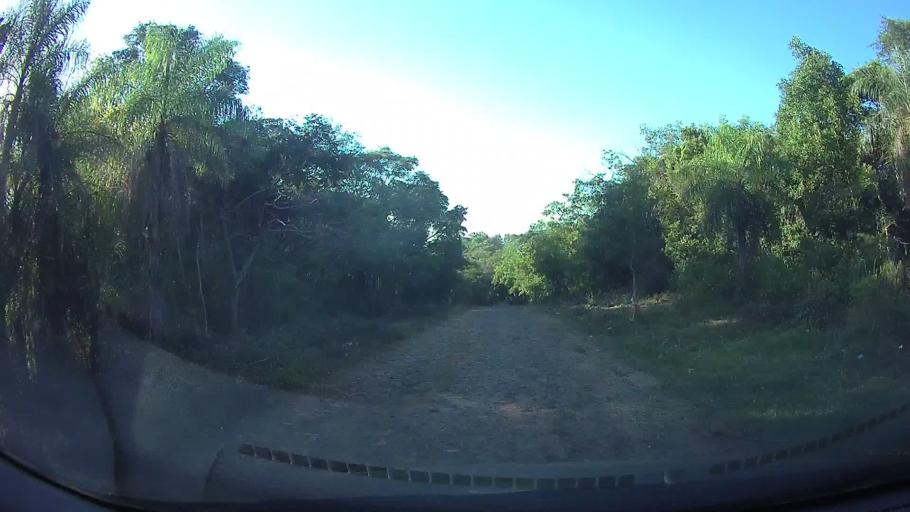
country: PY
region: Cordillera
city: San Bernardino
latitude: -25.3110
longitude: -57.2656
